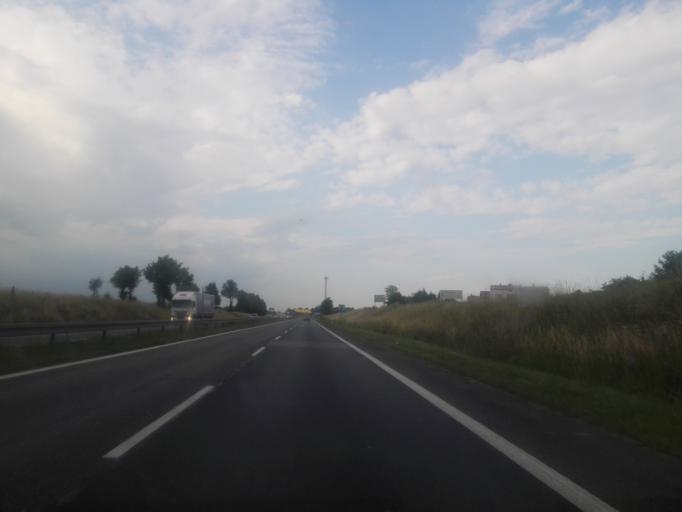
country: PL
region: Silesian Voivodeship
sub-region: Powiat myszkowski
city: Kozieglowy
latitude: 50.6025
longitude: 19.1522
